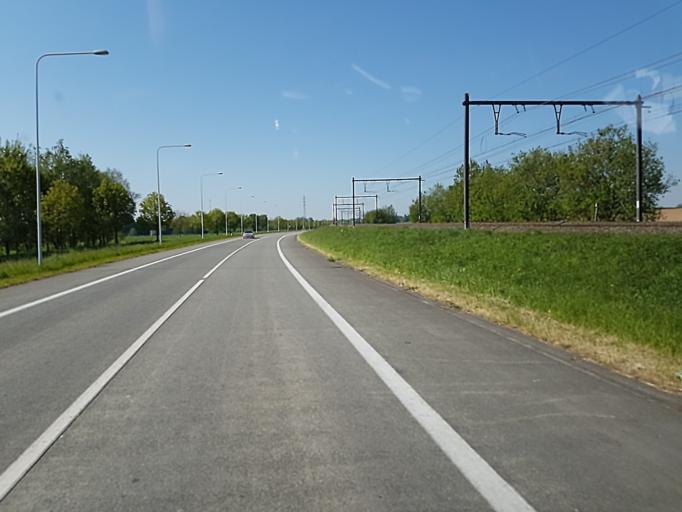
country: BE
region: Wallonia
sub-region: Province du Hainaut
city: Ath
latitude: 50.6495
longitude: 3.7853
